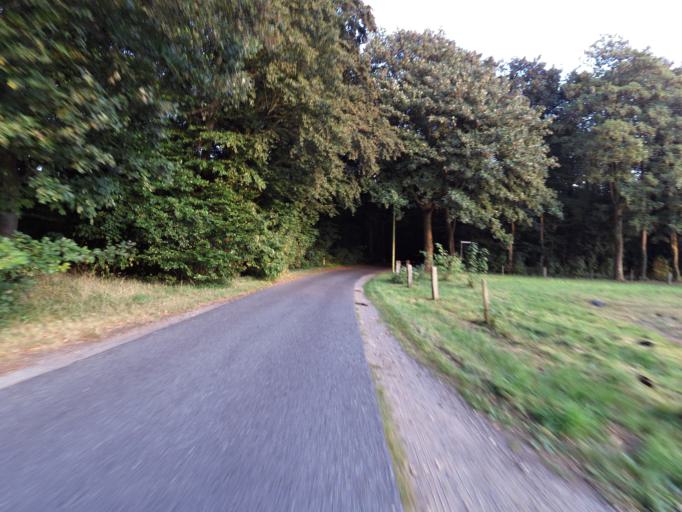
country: DE
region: North Rhine-Westphalia
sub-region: Regierungsbezirk Dusseldorf
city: Emmerich
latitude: 51.8586
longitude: 6.1956
